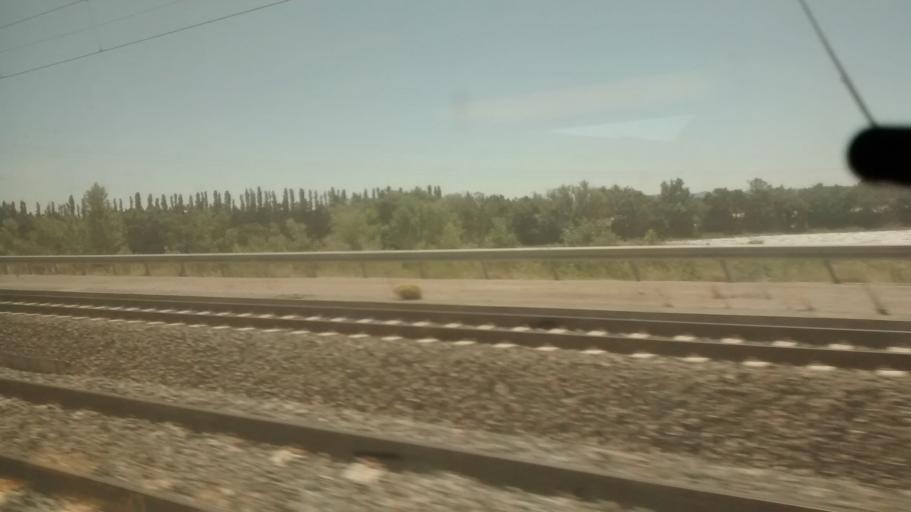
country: FR
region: Provence-Alpes-Cote d'Azur
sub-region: Departement du Vaucluse
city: Piolenc
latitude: 44.1572
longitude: 4.7432
